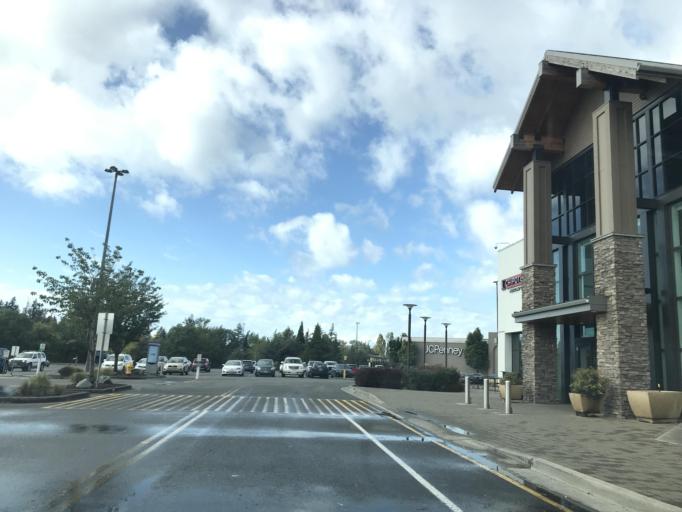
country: US
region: Washington
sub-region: Whatcom County
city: Bellingham
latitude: 48.7850
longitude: -122.4891
